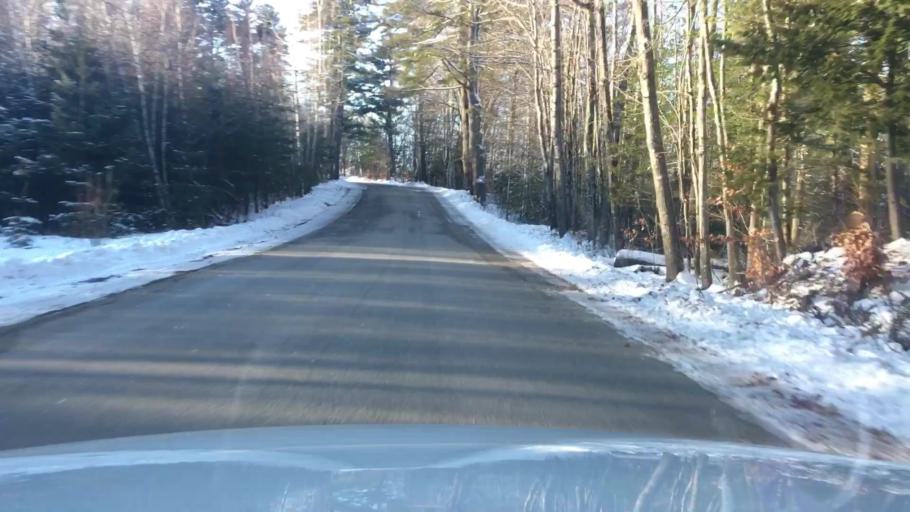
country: US
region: Maine
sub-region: Kennebec County
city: Belgrade
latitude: 44.4239
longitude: -69.8325
